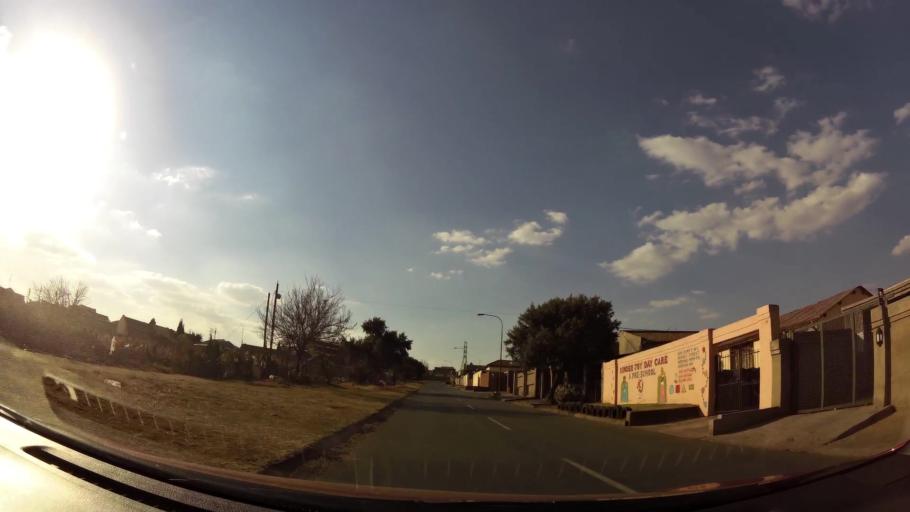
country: ZA
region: Gauteng
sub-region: City of Johannesburg Metropolitan Municipality
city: Roodepoort
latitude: -26.2046
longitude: 27.8785
